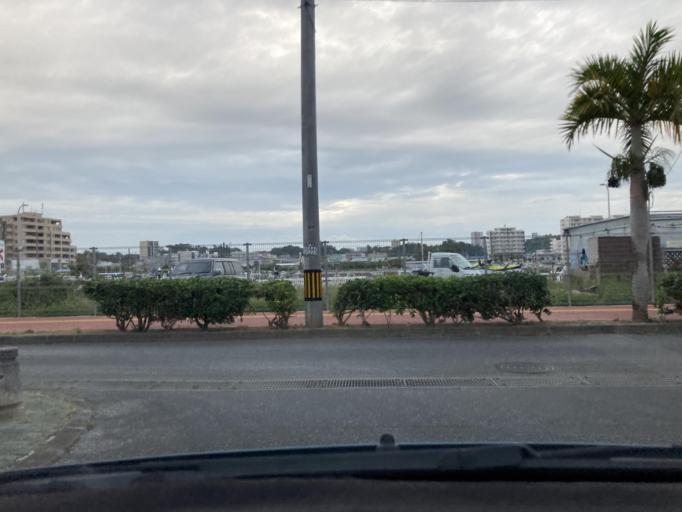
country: JP
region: Okinawa
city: Chatan
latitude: 26.3224
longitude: 127.7518
